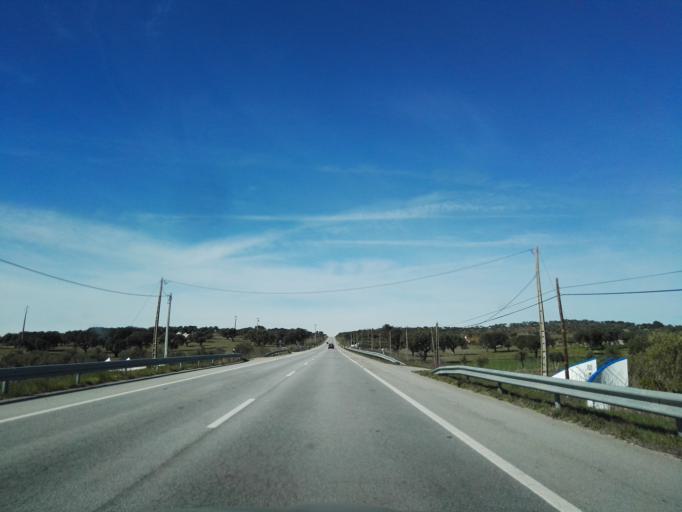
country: PT
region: Portalegre
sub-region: Arronches
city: Arronches
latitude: 39.1402
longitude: -7.2977
